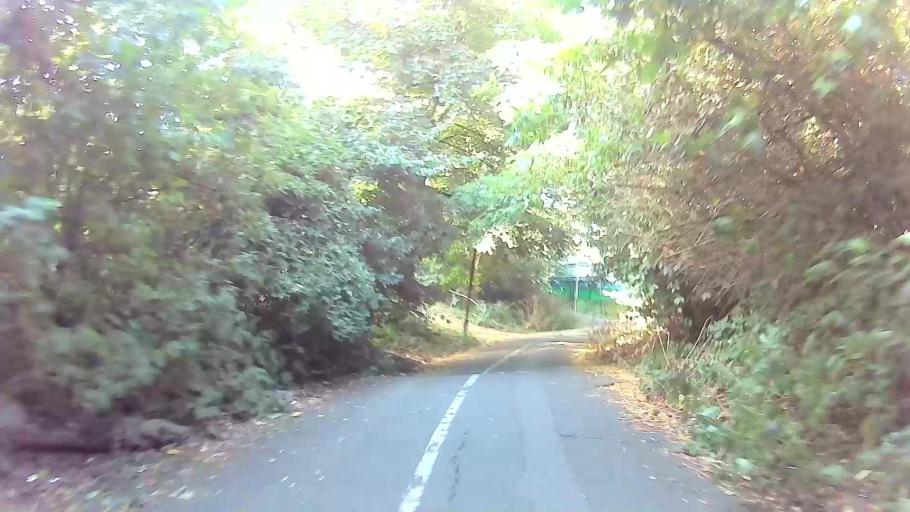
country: GB
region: England
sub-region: Greater London
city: East Ham
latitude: 51.5159
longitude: 0.0601
